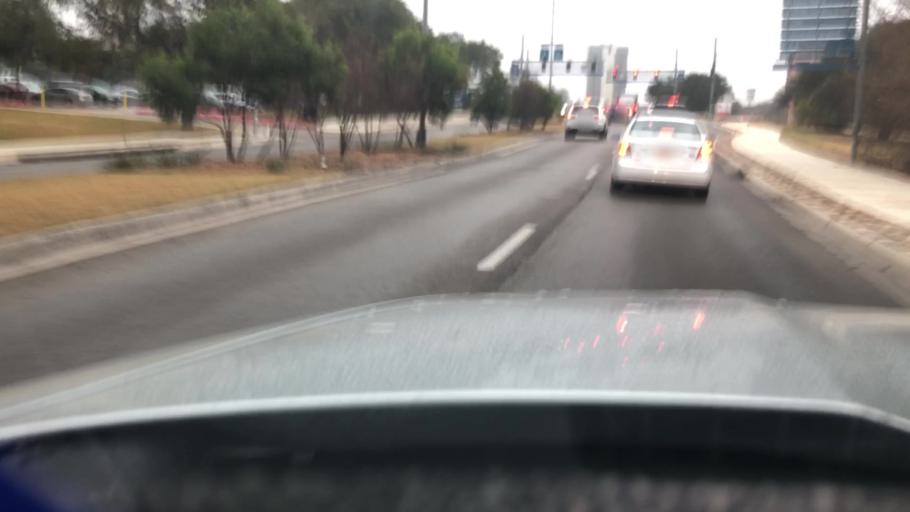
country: US
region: Texas
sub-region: Bexar County
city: Balcones Heights
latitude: 29.5146
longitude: -98.5776
